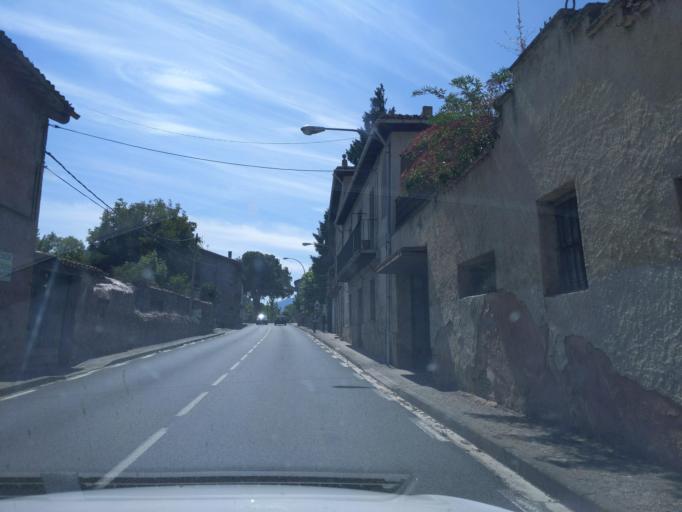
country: ES
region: La Rioja
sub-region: Provincia de La Rioja
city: Ojacastro
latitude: 42.3477
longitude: -3.0015
